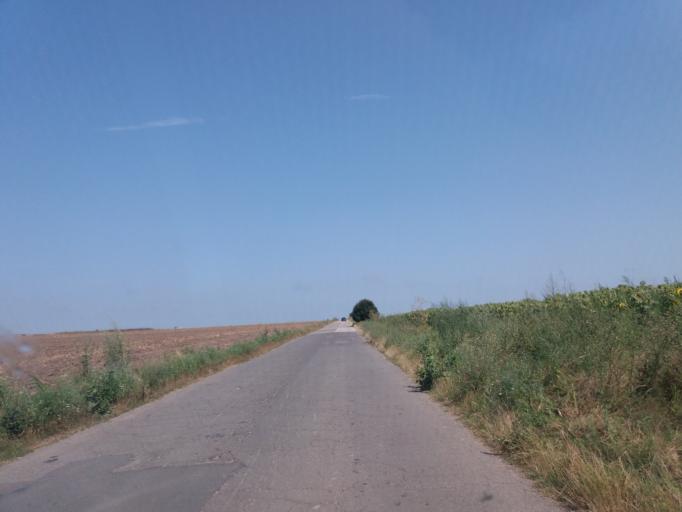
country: RO
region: Constanta
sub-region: Comuna Corbu
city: Corbu
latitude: 44.4239
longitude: 28.6778
